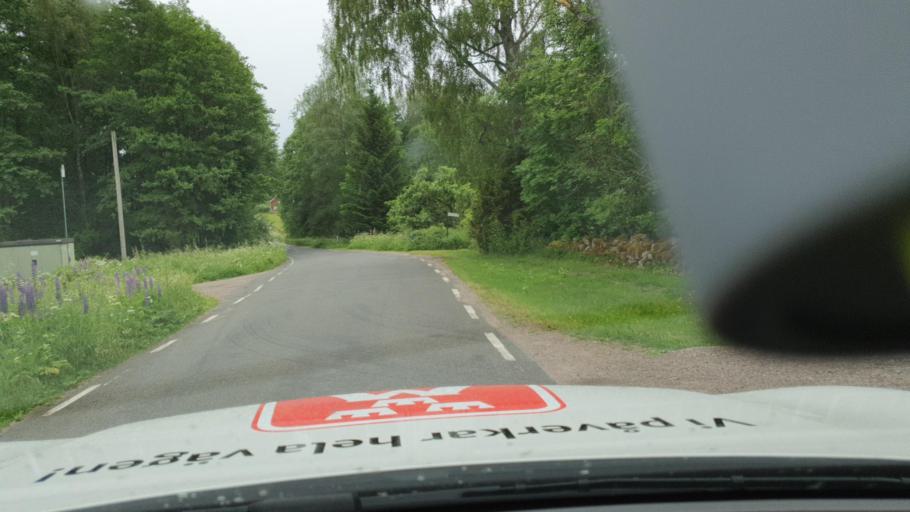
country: SE
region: Vaestra Goetaland
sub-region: Hjo Kommun
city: Hjo
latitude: 58.3160
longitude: 14.1840
